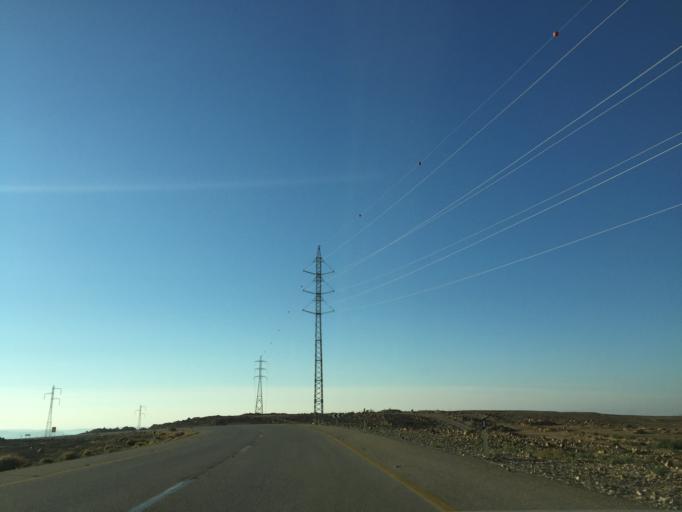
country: IL
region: Southern District
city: Mitzpe Ramon
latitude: 30.5102
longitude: 34.9404
